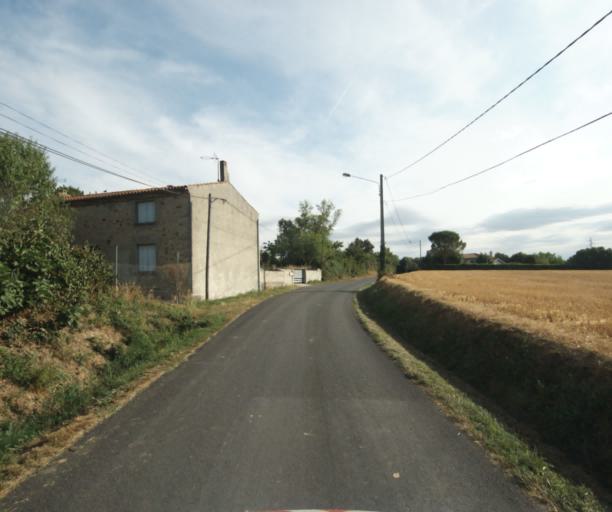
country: FR
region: Midi-Pyrenees
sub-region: Departement de la Haute-Garonne
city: Revel
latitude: 43.4523
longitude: 1.9700
